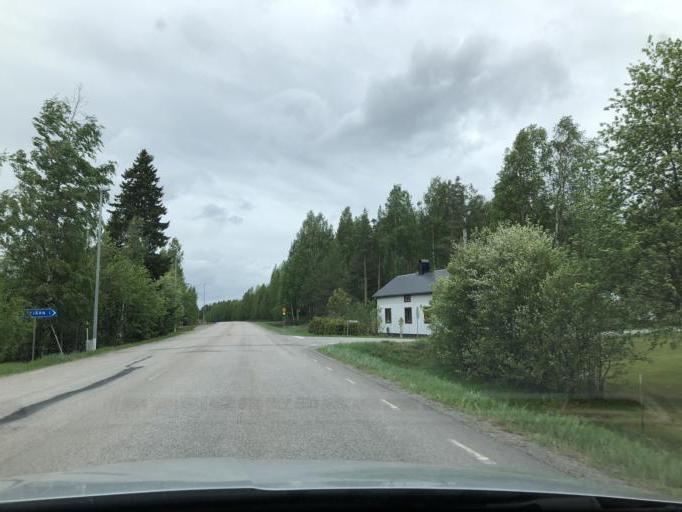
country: SE
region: Norrbotten
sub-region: Pitea Kommun
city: Bergsviken
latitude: 65.3807
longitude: 21.3396
